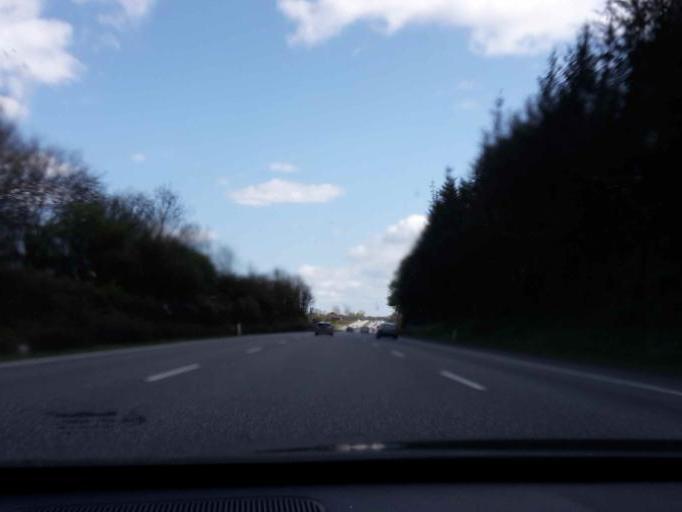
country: DK
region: South Denmark
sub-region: Fredericia Kommune
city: Snoghoj
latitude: 55.5393
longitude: 9.6703
